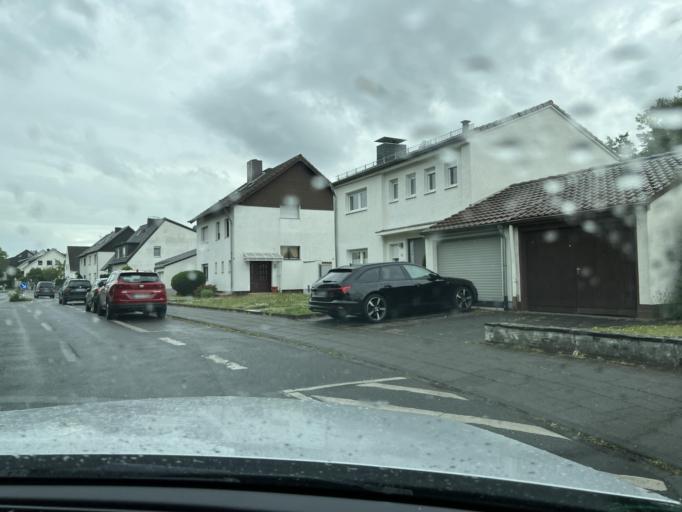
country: DE
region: North Rhine-Westphalia
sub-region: Regierungsbezirk Koln
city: Rath
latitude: 50.9252
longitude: 7.0873
